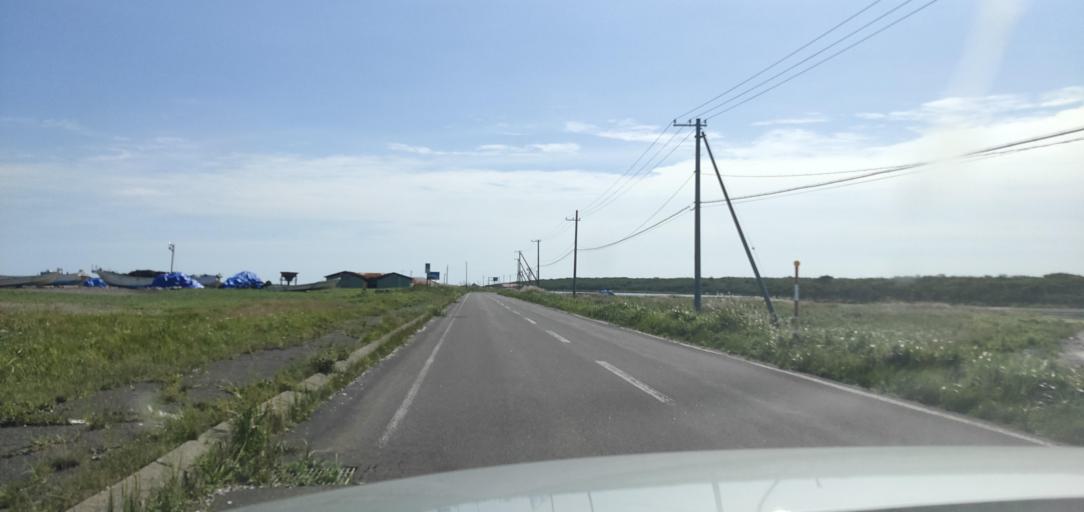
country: JP
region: Hokkaido
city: Shibetsu
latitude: 43.6108
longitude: 145.2673
